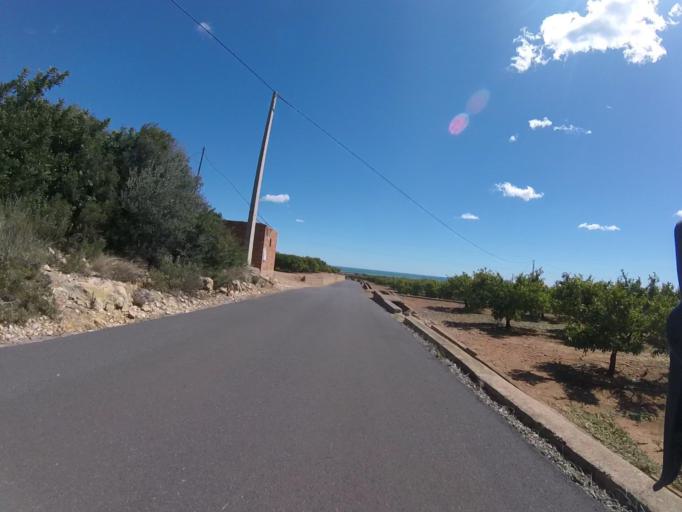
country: ES
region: Valencia
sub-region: Provincia de Castello
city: Orpesa/Oropesa del Mar
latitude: 40.1664
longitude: 0.1498
